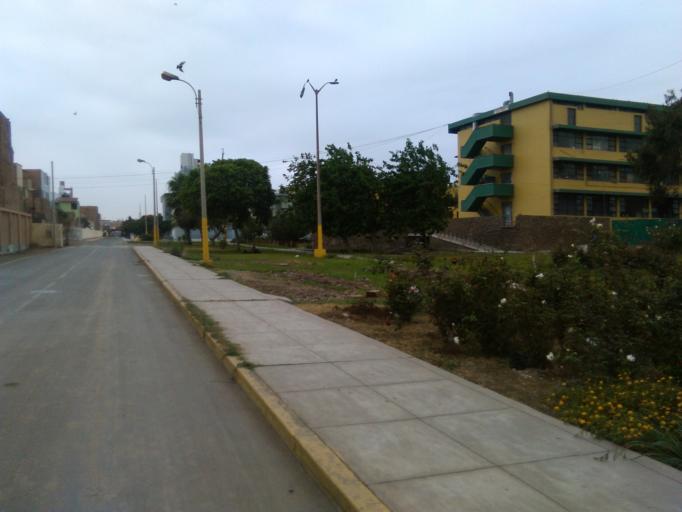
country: PE
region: Callao
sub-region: Callao
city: Callao
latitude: -12.0546
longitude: -77.0879
